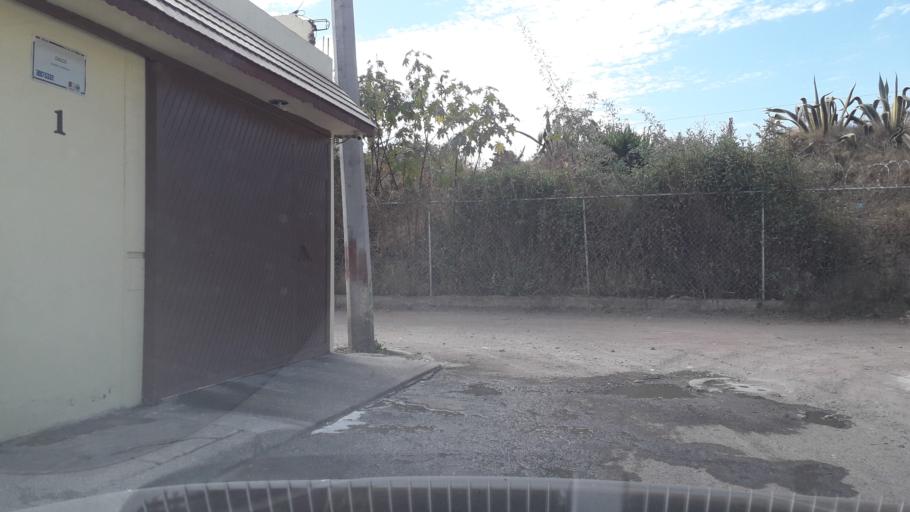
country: MX
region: Mexico City
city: Gustavo A. Madero
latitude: 19.5083
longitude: -99.0860
